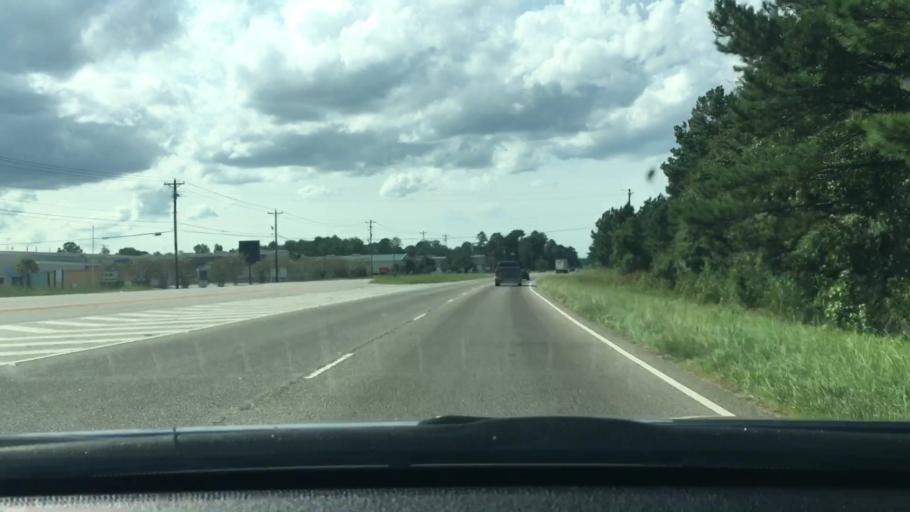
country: US
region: South Carolina
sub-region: Richland County
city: Forest Acres
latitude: 33.9426
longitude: -80.9594
